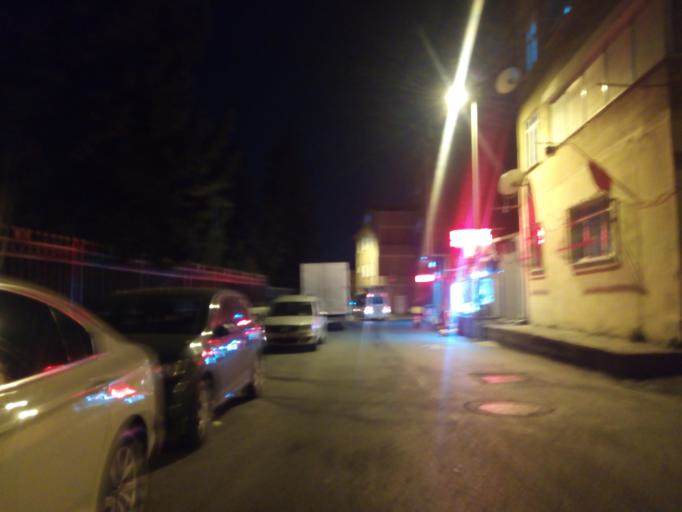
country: TR
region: Istanbul
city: Zeytinburnu
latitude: 41.0129
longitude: 28.9175
